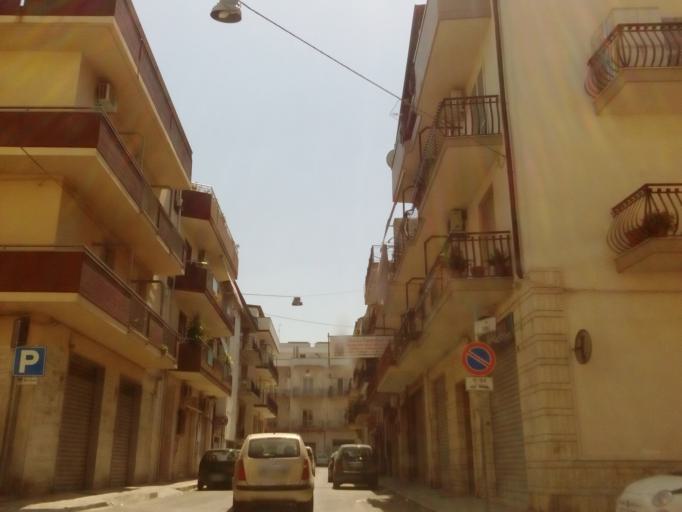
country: IT
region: Apulia
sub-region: Provincia di Bari
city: Gravina in Puglia
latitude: 40.8190
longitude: 16.4271
